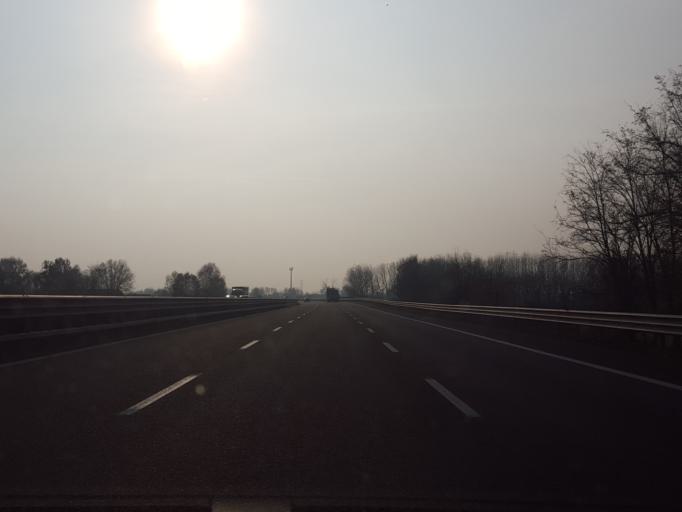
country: IT
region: Veneto
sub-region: Provincia di Treviso
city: Lughignano
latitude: 45.6299
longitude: 12.3074
